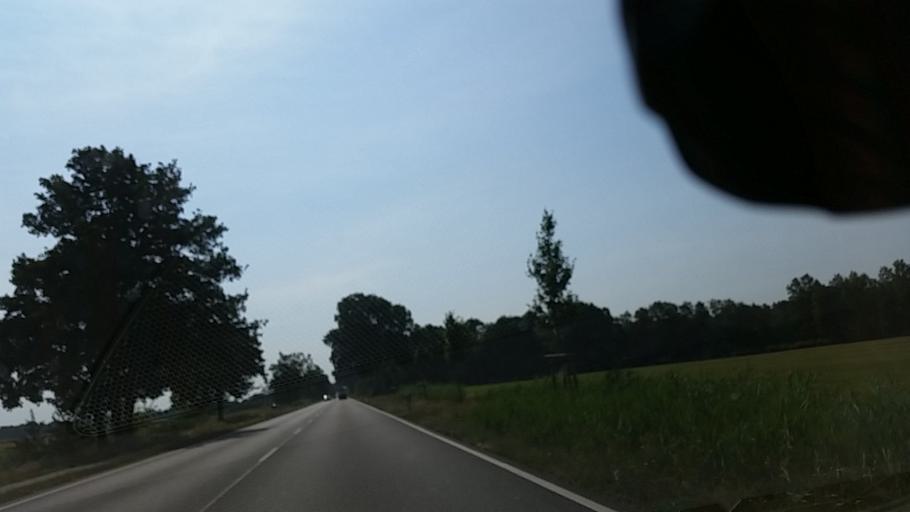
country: DE
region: Lower Saxony
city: Diepholz
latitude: 52.6121
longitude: 8.3206
